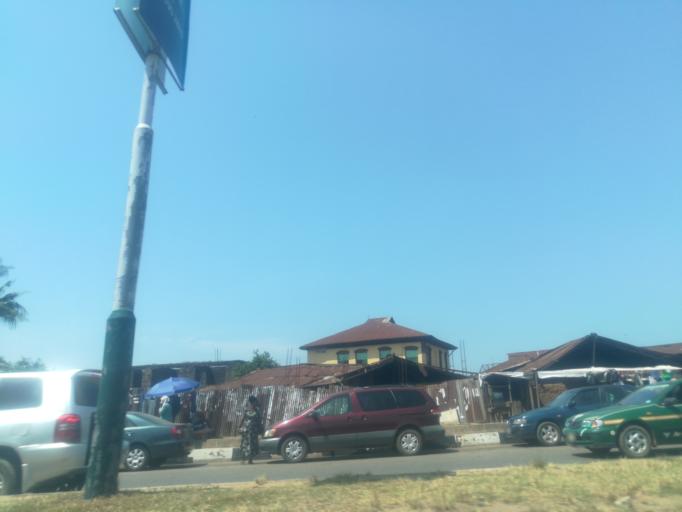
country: NG
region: Ogun
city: Abeokuta
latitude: 7.1554
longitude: 3.3475
